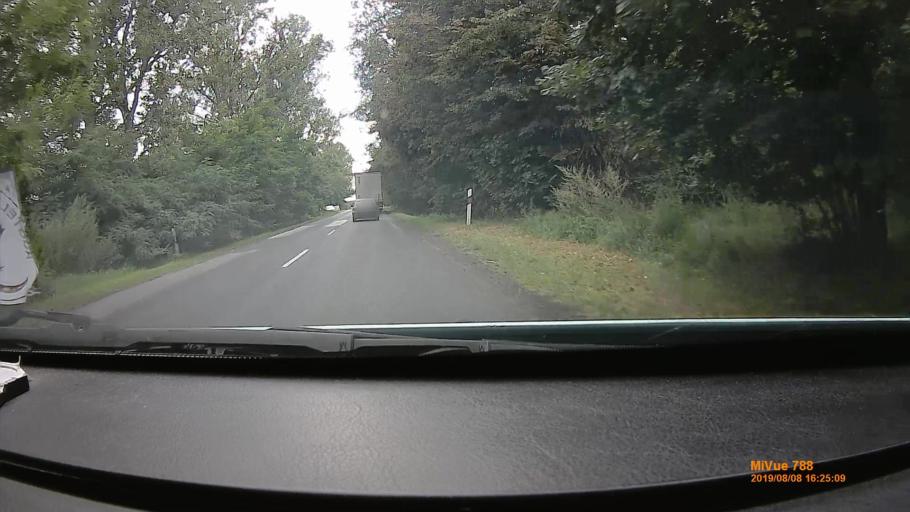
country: HU
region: Szabolcs-Szatmar-Bereg
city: Hodasz
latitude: 47.9688
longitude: 22.2180
